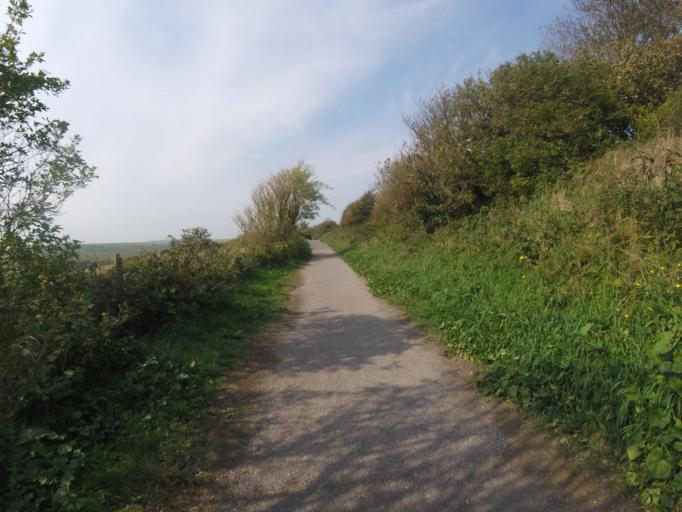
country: GB
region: England
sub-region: East Sussex
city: Portslade
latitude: 50.8574
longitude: -0.1980
